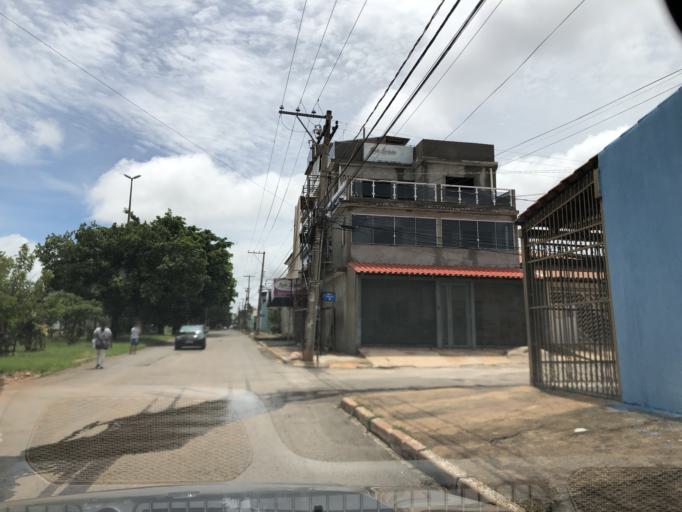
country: BR
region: Federal District
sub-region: Brasilia
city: Brasilia
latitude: -15.7981
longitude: -48.1240
